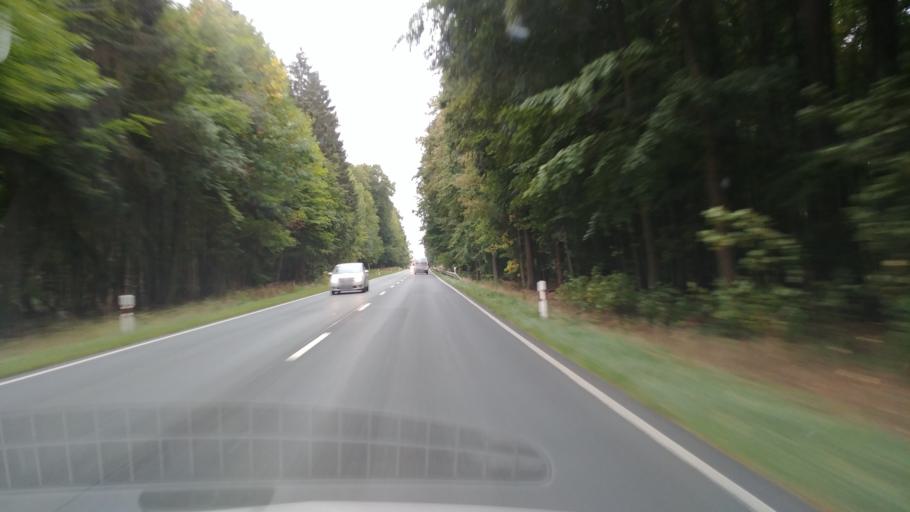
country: DE
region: Rheinland-Pfalz
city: Kaltenholzhausen
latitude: 50.2805
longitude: 8.1672
